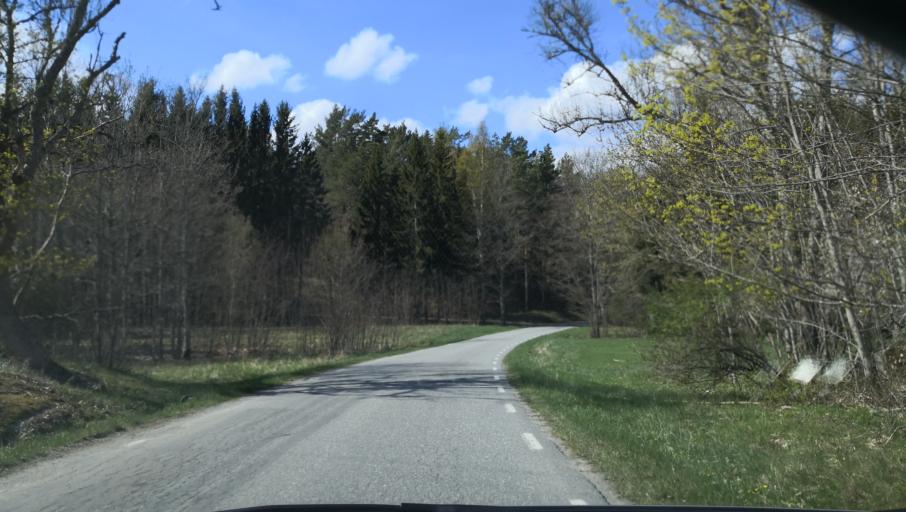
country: SE
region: Stockholm
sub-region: Varmdo Kommun
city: Hemmesta
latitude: 59.4094
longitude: 18.4958
